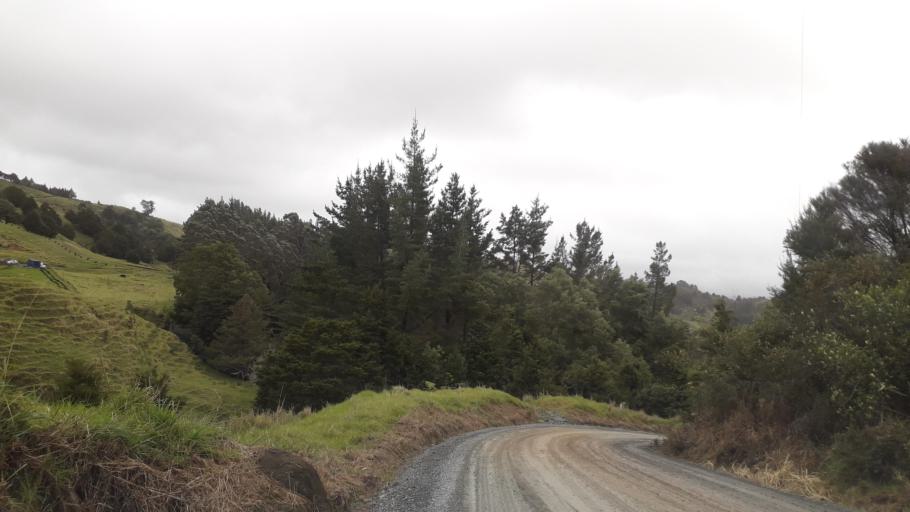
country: NZ
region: Northland
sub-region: Far North District
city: Kerikeri
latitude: -35.1280
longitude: 173.7436
